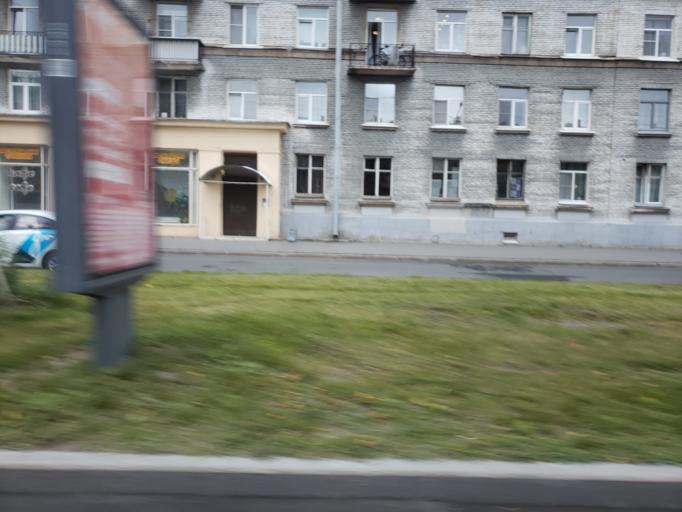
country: RU
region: St.-Petersburg
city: Vasyl'evsky Ostrov
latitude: 59.9360
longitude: 30.2340
